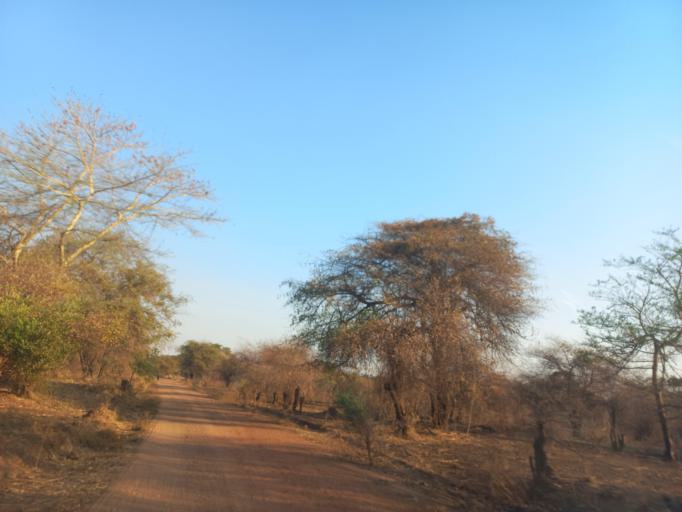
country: ZM
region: Lusaka
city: Luangwa
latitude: -15.4307
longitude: 30.3420
